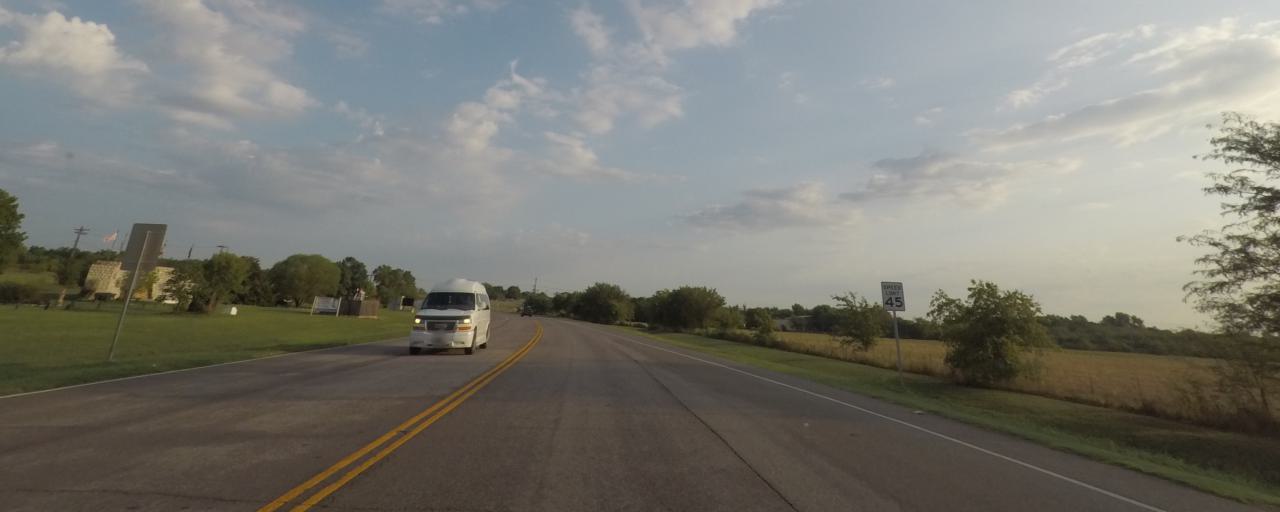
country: US
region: Oklahoma
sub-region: Stephens County
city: Comanche
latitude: 34.3737
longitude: -97.9642
